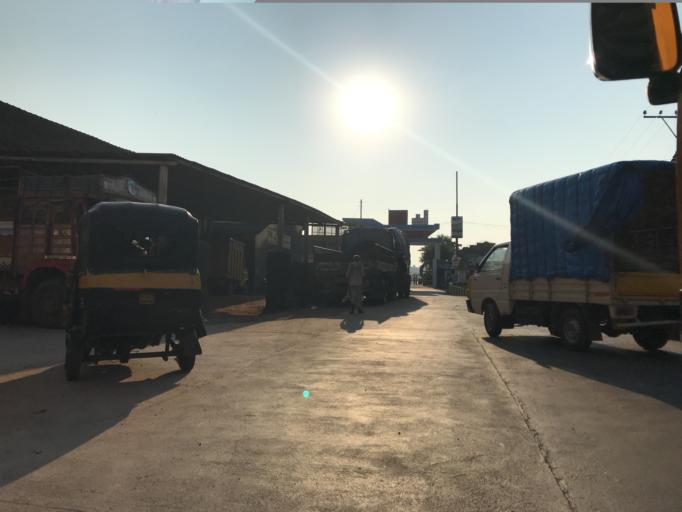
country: IN
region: Karnataka
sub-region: Dakshina Kannada
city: Ullal
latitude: 12.8616
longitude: 74.8331
